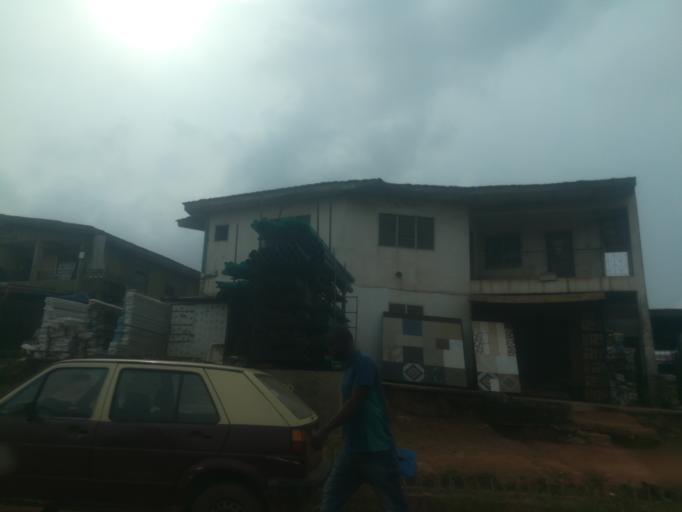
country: NG
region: Oyo
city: Ibadan
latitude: 7.4035
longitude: 3.9414
